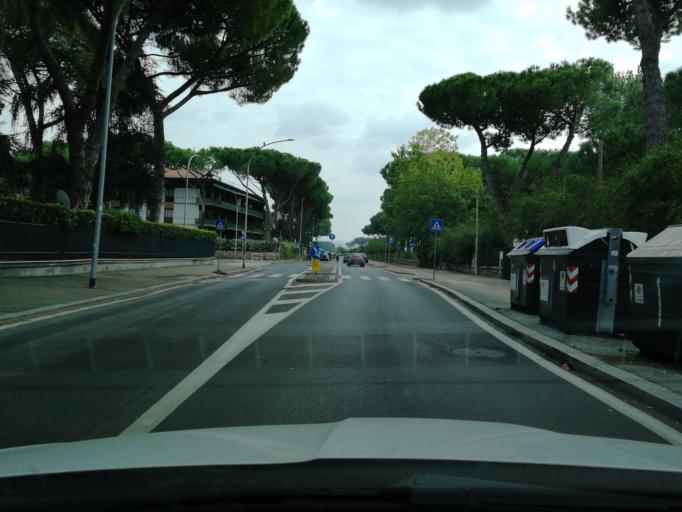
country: IT
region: Latium
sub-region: Citta metropolitana di Roma Capitale
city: Rome
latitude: 41.8499
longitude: 12.5615
